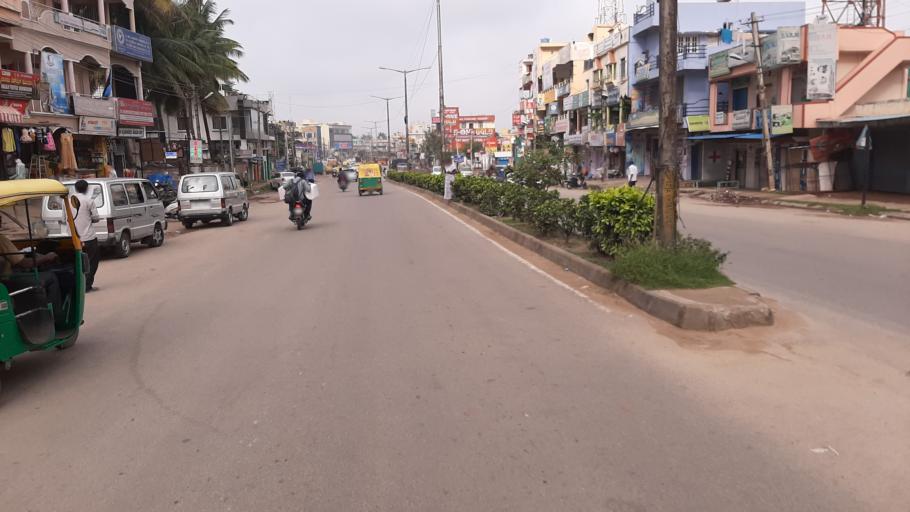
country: IN
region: Karnataka
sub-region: Bangalore Urban
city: Bangalore
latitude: 12.9859
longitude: 77.4872
